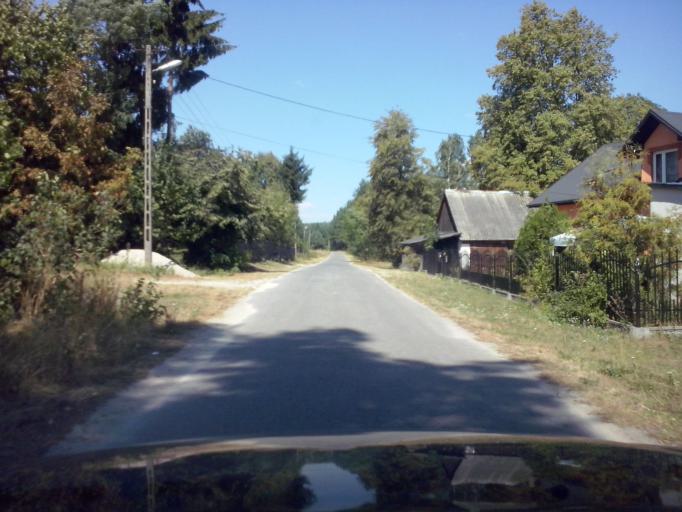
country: PL
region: Swietokrzyskie
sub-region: Powiat buski
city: Gnojno
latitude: 50.6266
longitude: 20.8736
